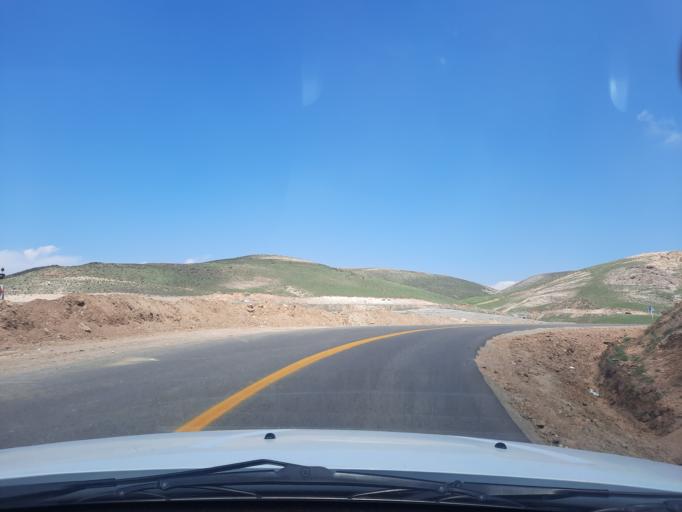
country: IR
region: Qazvin
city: Qazvin
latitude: 36.3876
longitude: 50.2075
